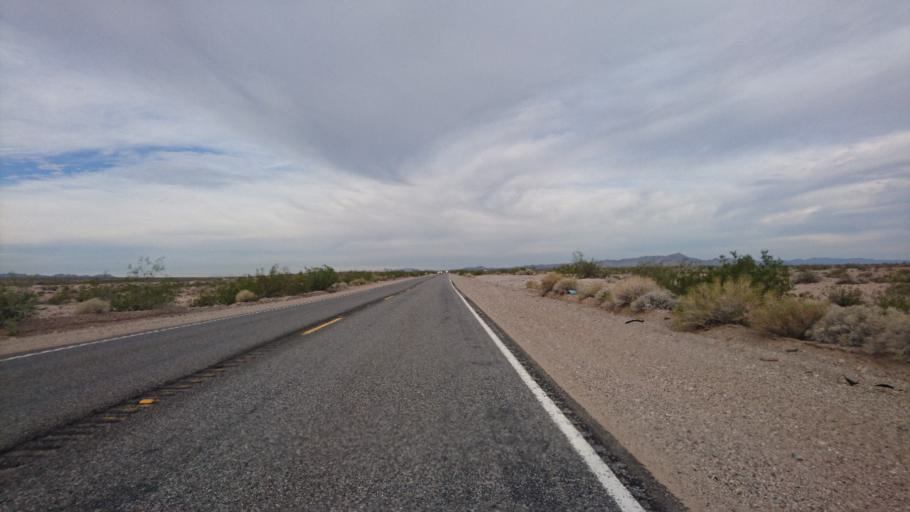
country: US
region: Arizona
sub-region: Mohave County
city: Willow Valley
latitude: 34.9334
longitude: -114.7987
